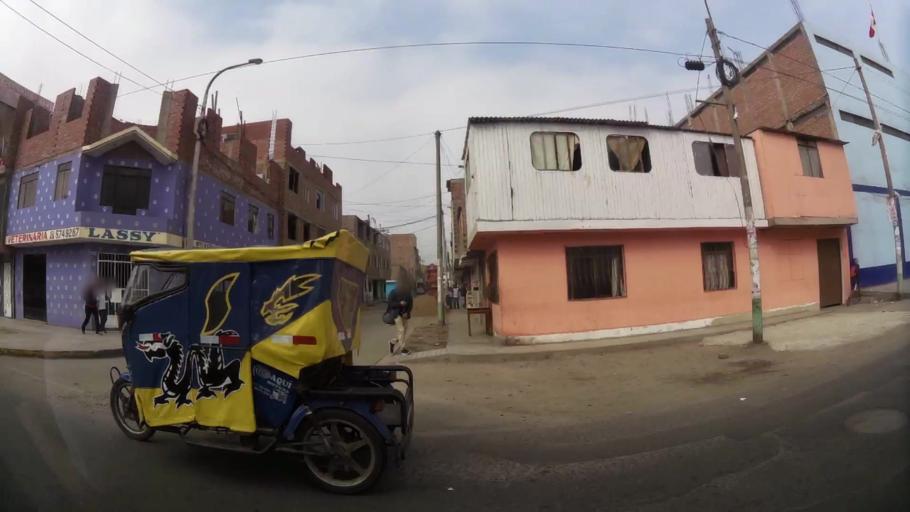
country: PE
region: Callao
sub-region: Callao
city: Callao
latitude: -12.0266
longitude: -77.0943
